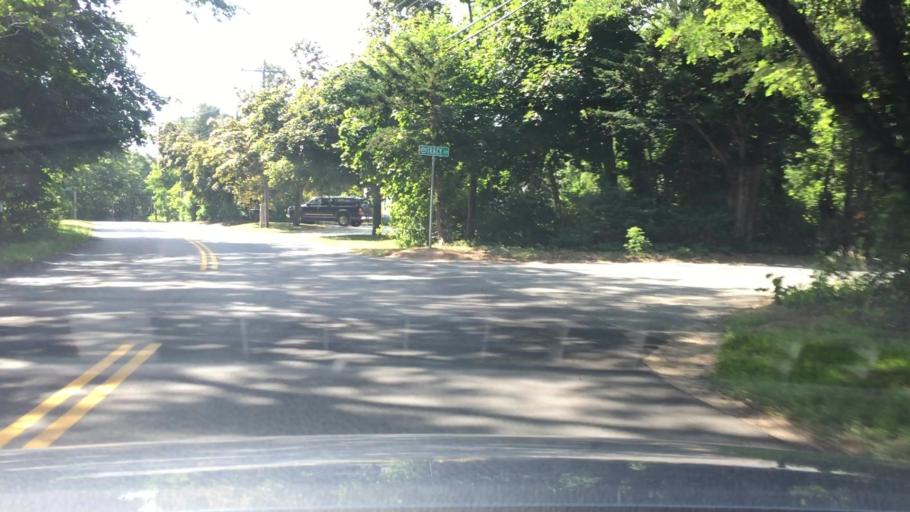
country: US
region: Massachusetts
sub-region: Barnstable County
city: North Eastham
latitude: 41.8578
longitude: -69.9716
